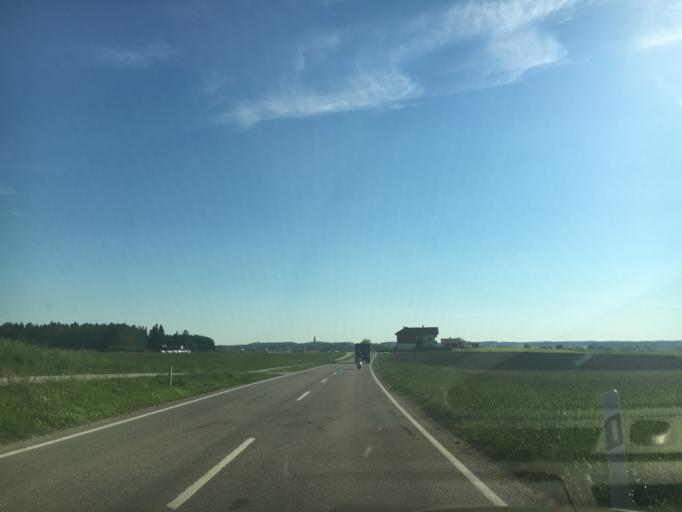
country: DE
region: Bavaria
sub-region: Upper Bavaria
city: Nussdorf
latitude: 47.9251
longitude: 12.5859
